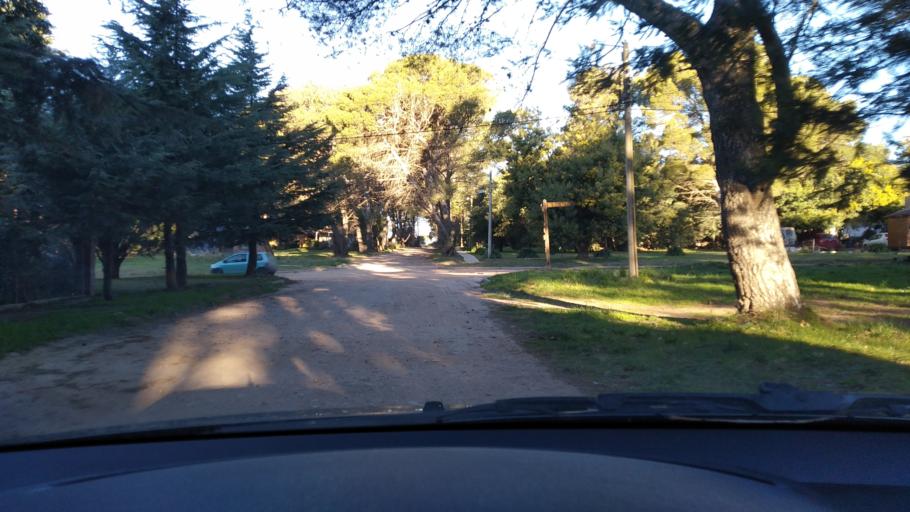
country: AR
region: Buenos Aires
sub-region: Partido de Tornquist
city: Tornquist
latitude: -38.0839
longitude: -61.9334
